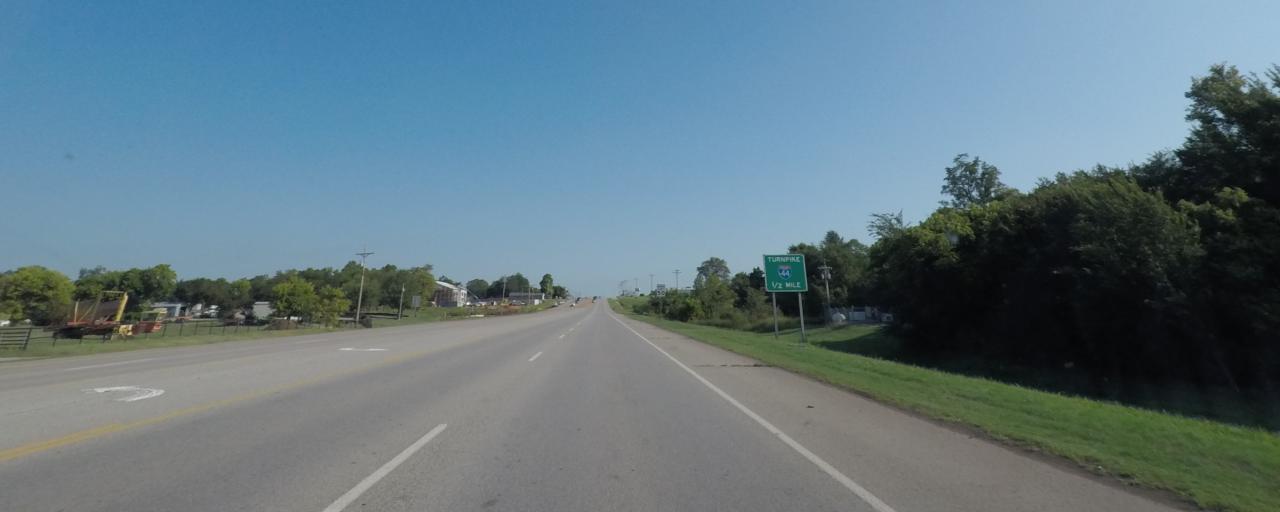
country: US
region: Oklahoma
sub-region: McClain County
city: Newcastle
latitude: 35.2671
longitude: -97.6001
